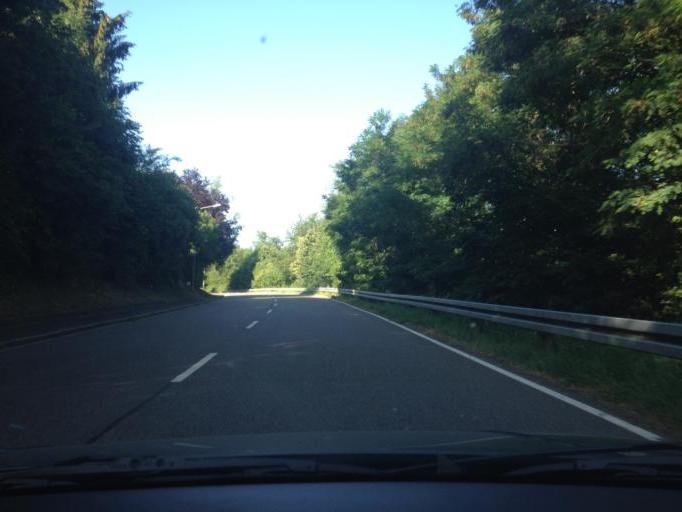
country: DE
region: Saarland
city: Ottweiler
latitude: 49.4064
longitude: 7.1690
